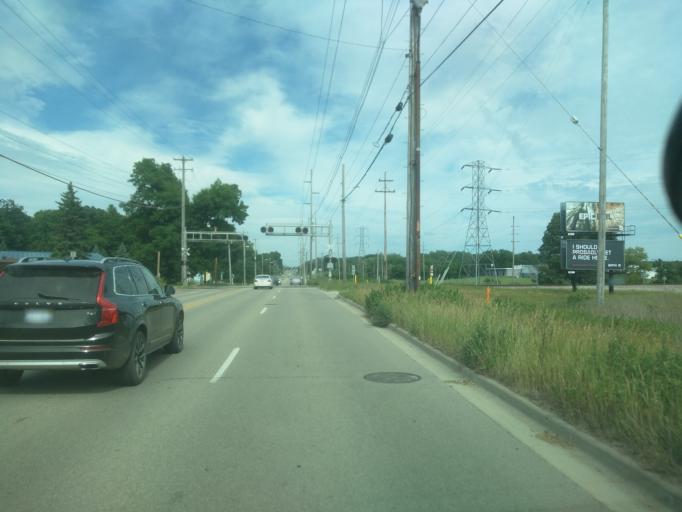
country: US
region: Michigan
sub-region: Ingham County
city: Holt
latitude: 42.6829
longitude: -84.5304
